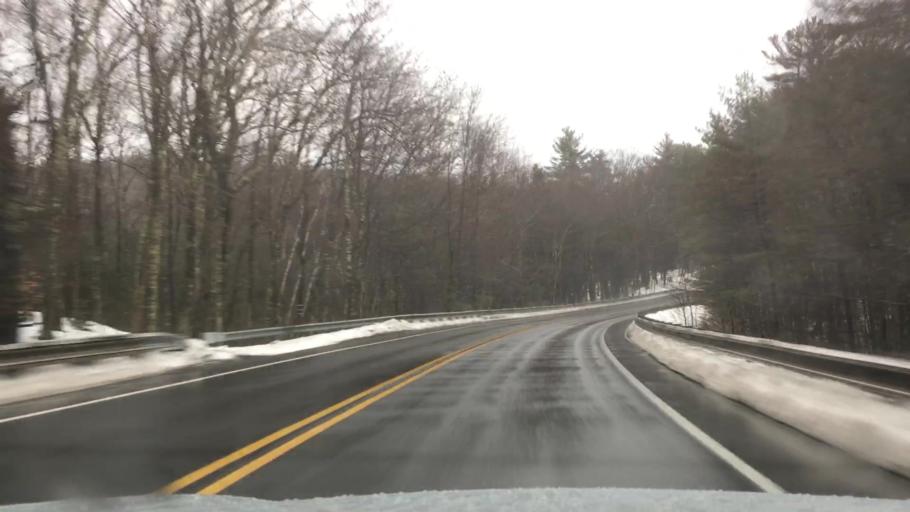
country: US
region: Massachusetts
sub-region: Hampshire County
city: Pelham
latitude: 42.4201
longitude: -72.3995
